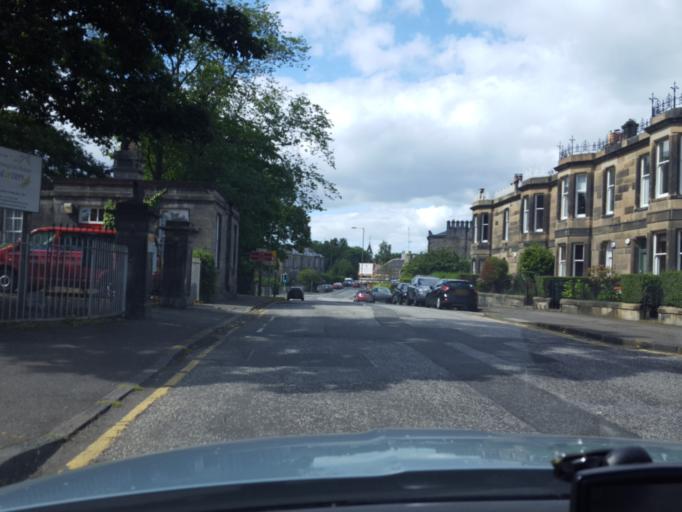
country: GB
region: Scotland
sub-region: Edinburgh
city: Edinburgh
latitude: 55.9759
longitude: -3.1914
